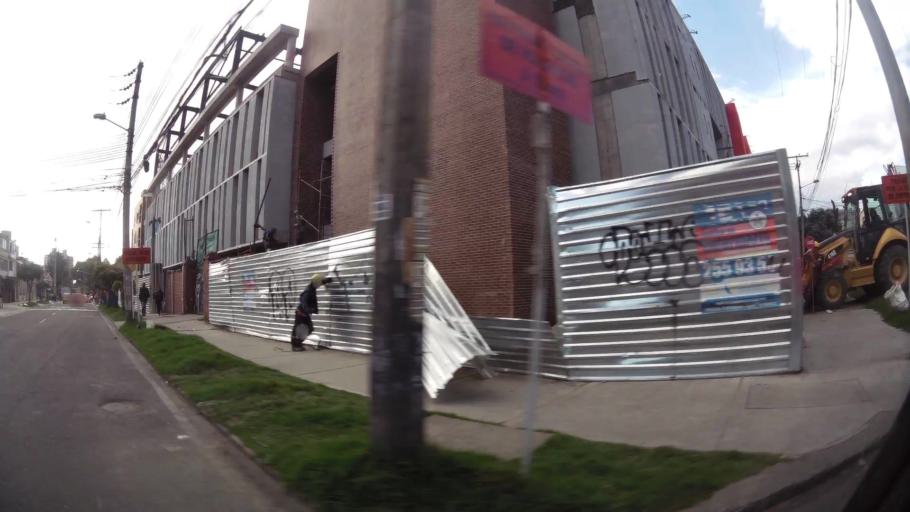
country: CO
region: Bogota D.C.
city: Bogota
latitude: 4.6476
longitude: -74.0673
